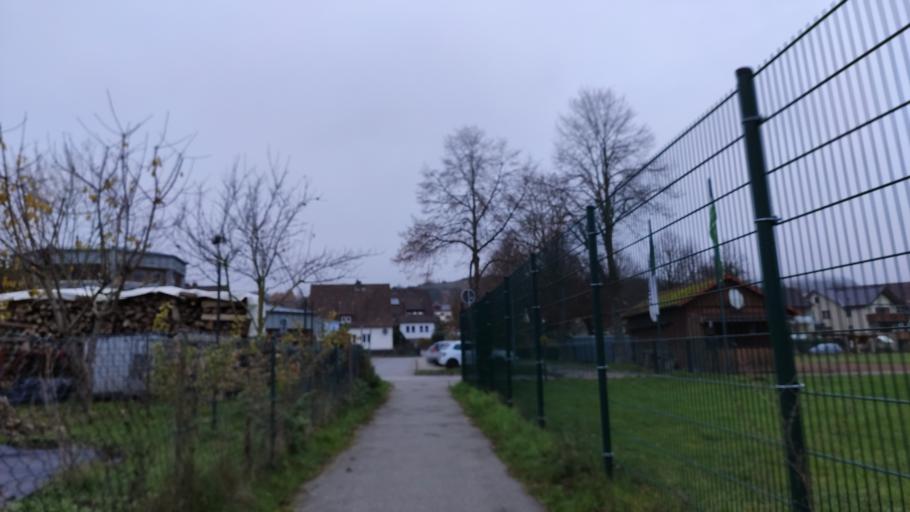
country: DE
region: North Rhine-Westphalia
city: Beverungen
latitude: 51.7083
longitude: 9.2959
